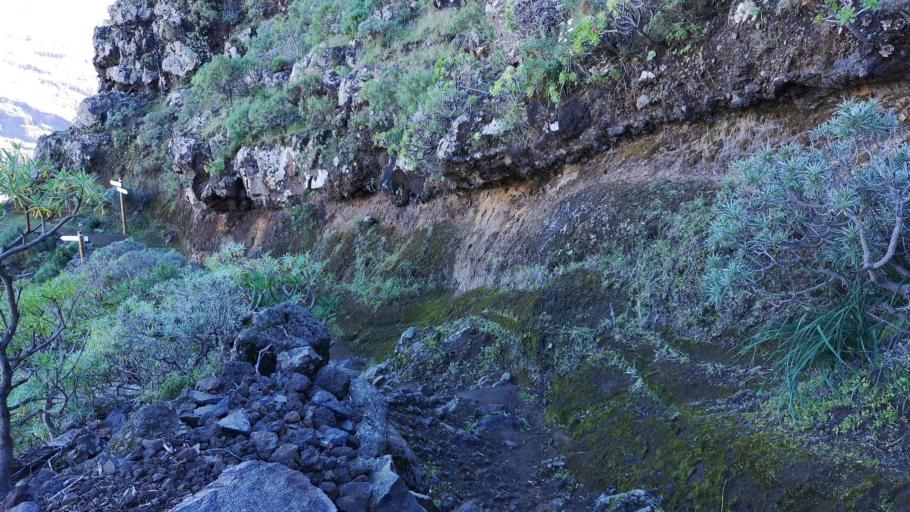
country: ES
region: Canary Islands
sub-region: Provincia de Santa Cruz de Tenerife
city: Alajero
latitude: 28.0809
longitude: -17.2263
